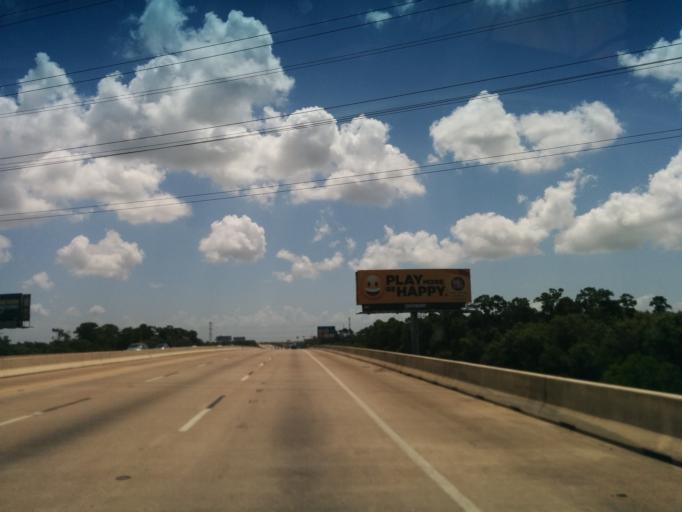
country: US
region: Texas
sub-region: Chambers County
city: Mont Belvieu
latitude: 29.8212
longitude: -94.9158
